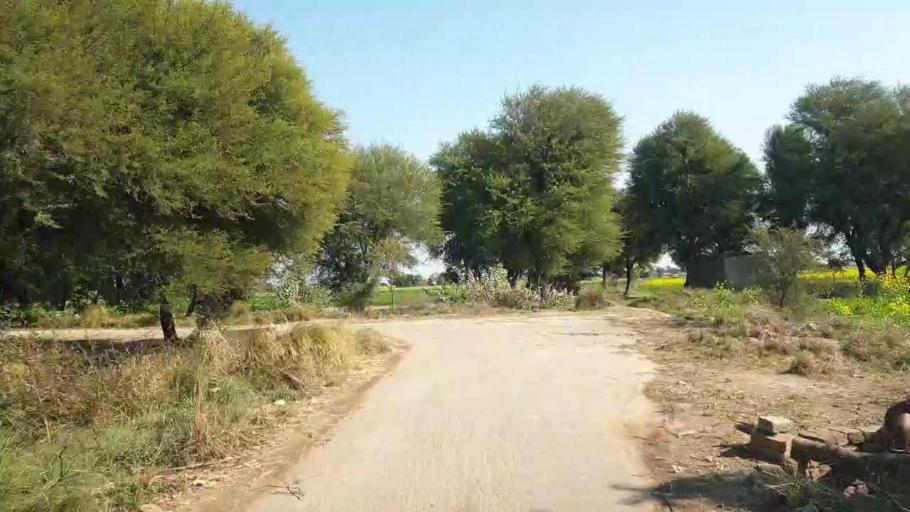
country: PK
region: Sindh
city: Shahpur Chakar
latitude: 26.0786
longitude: 68.5840
